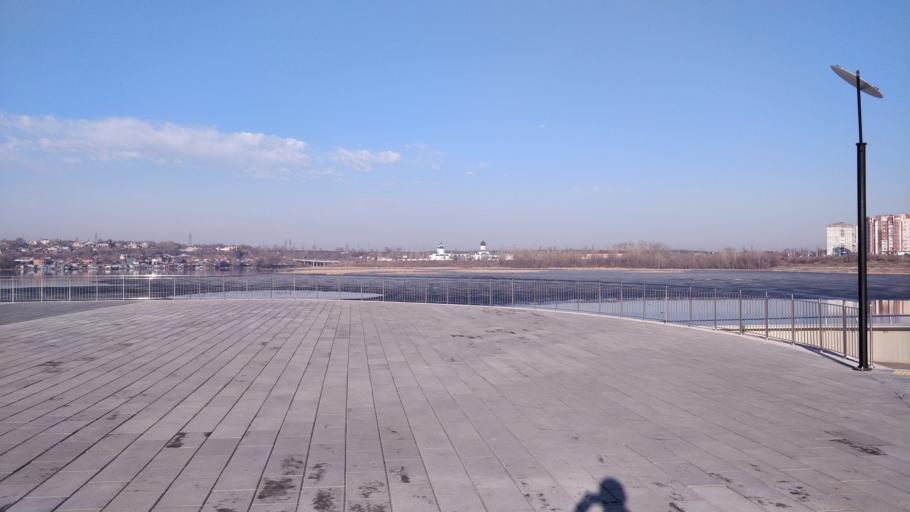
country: RU
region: Samara
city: Syzran'
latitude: 53.1479
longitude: 48.4527
